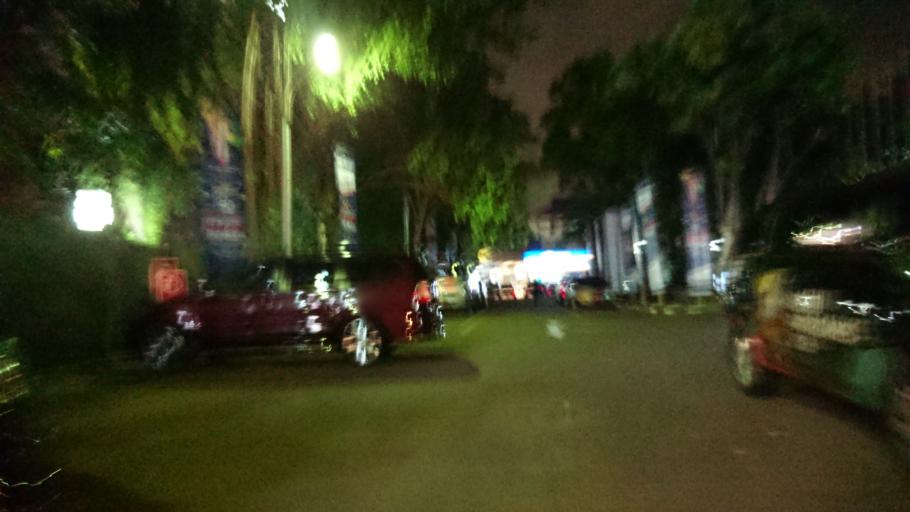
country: ID
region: Jakarta Raya
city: Jakarta
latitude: -6.2139
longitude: 106.7992
